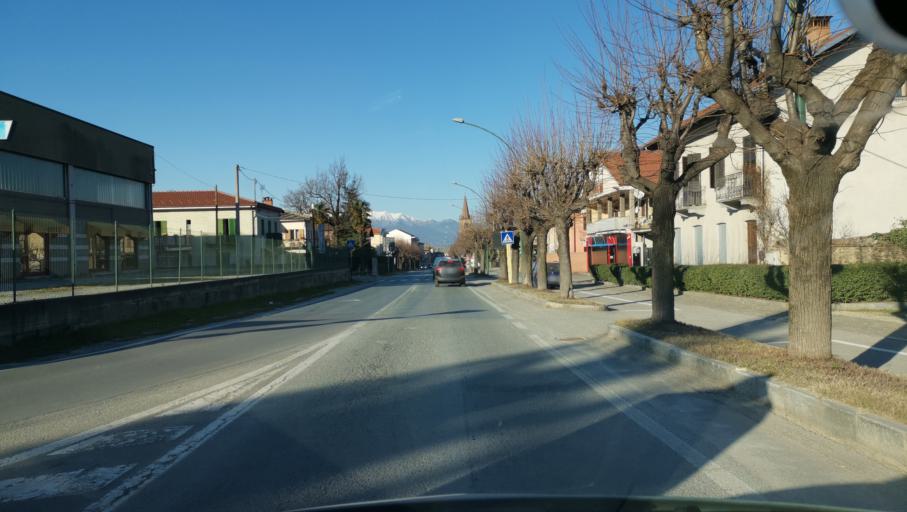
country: IT
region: Piedmont
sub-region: Provincia di Cuneo
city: Bagnolo Piemonte
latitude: 44.7574
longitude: 7.3139
